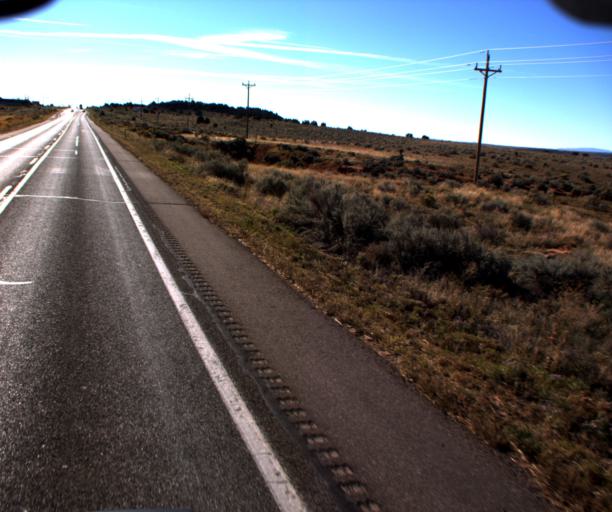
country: US
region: Arizona
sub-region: Mohave County
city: Colorado City
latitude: 36.9749
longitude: -112.9786
